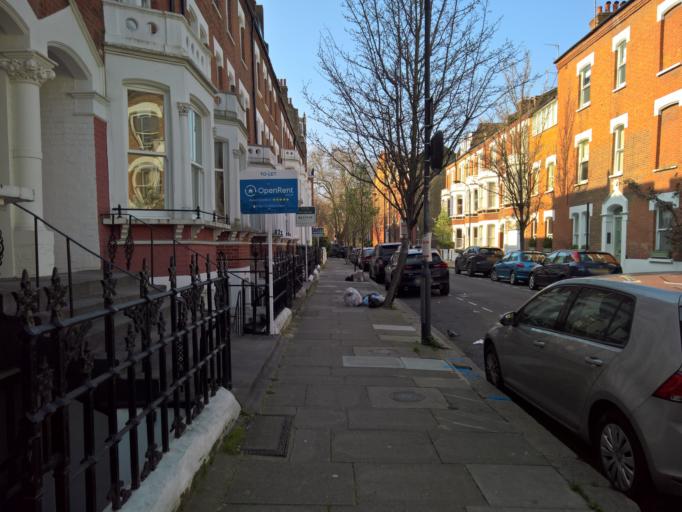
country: GB
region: England
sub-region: Greater London
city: Hammersmith
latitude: 51.4964
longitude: -0.2169
